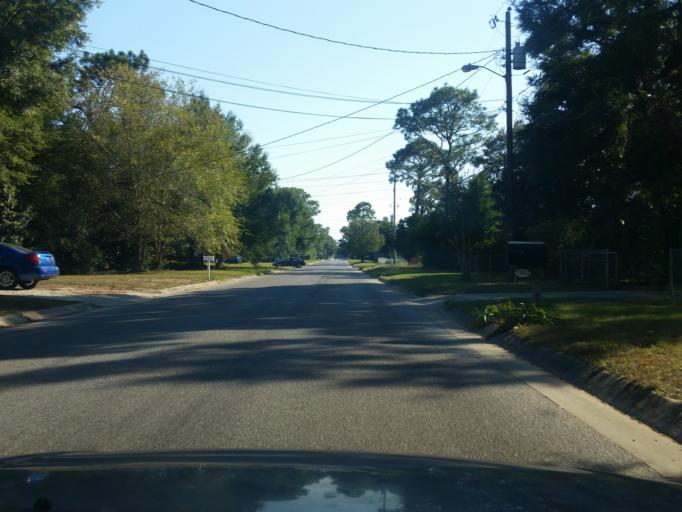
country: US
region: Florida
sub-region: Escambia County
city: Ferry Pass
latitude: 30.4982
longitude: -87.2008
